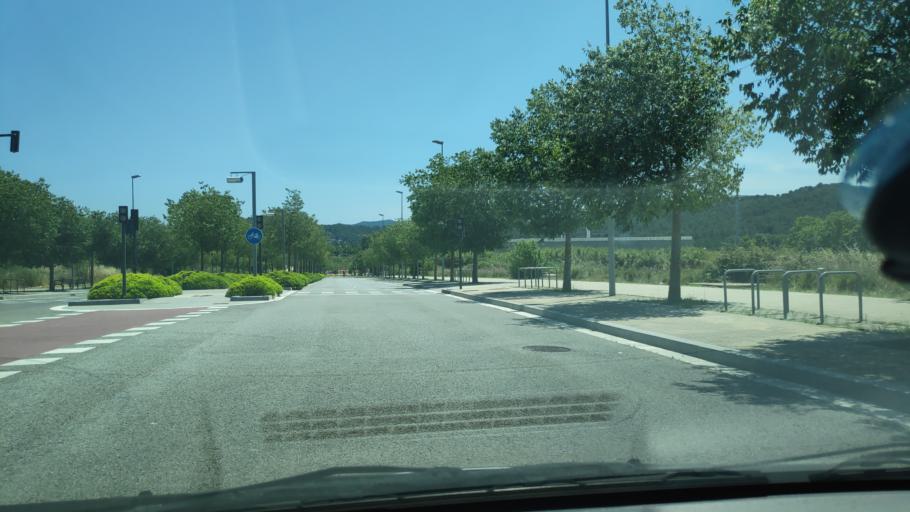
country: ES
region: Catalonia
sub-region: Provincia de Barcelona
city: Cerdanyola del Valles
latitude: 41.4885
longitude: 2.1122
